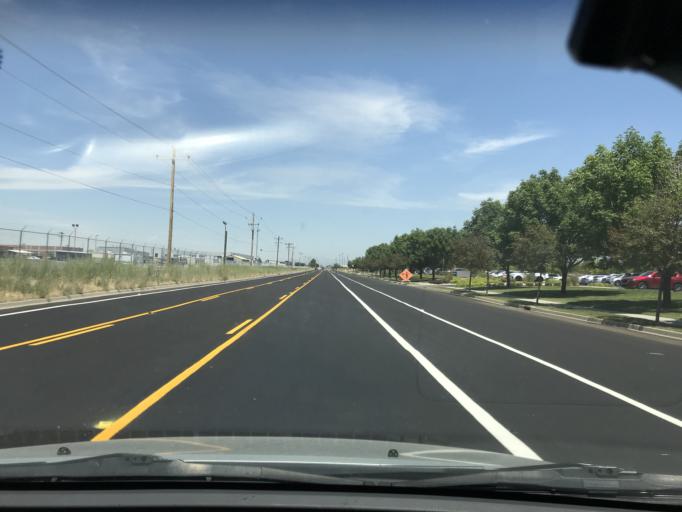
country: US
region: Utah
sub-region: Salt Lake County
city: Salt Lake City
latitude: 40.7895
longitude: -111.9536
